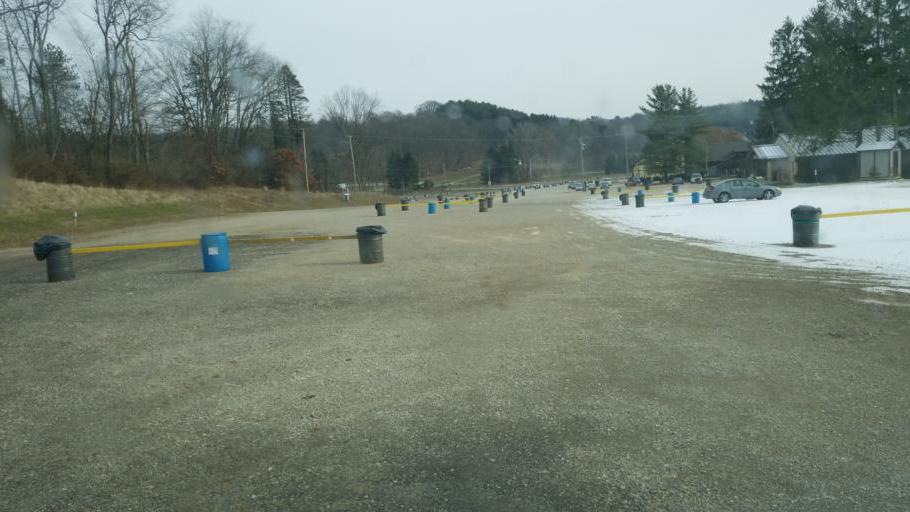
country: US
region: Ohio
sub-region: Sandusky County
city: Bellville
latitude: 40.6730
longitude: -82.5030
